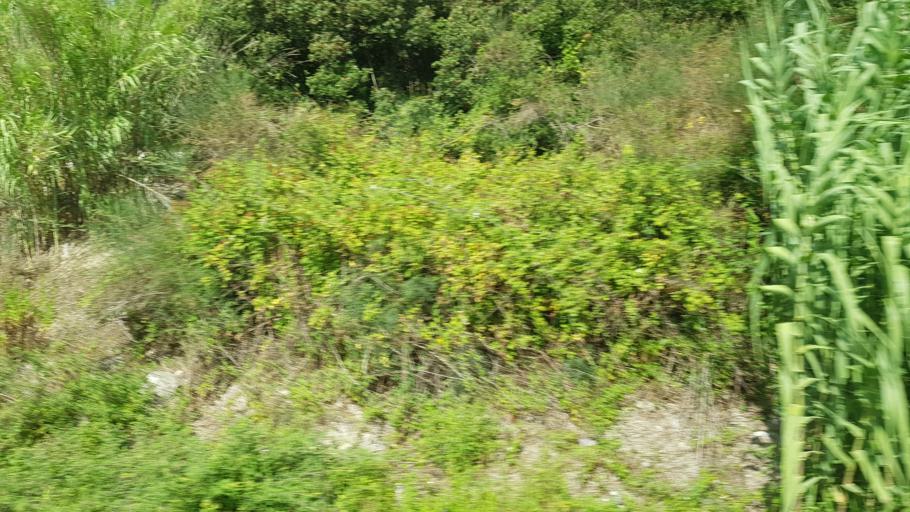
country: AL
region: Vlore
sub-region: Rrethi i Delvines
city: Mesopotam
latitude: 39.9029
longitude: 20.0851
